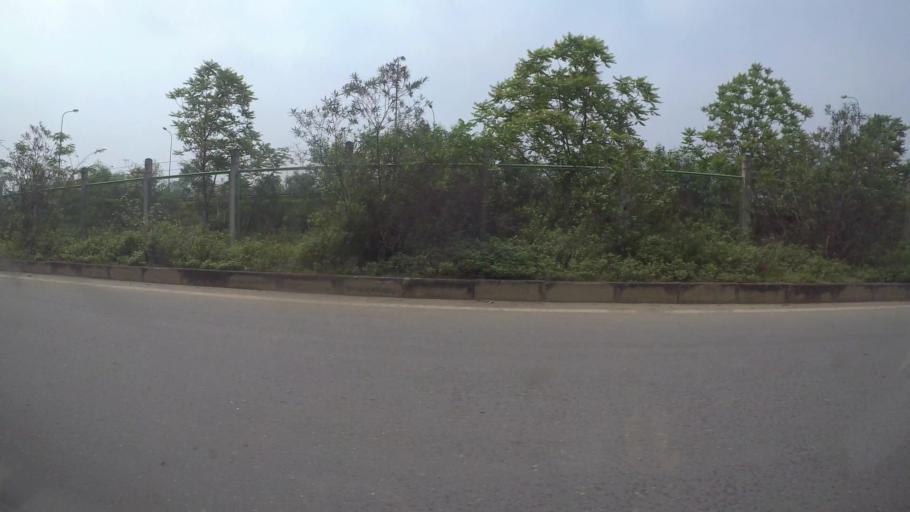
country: VN
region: Ha Noi
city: Lien Quan
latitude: 20.9899
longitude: 105.5653
